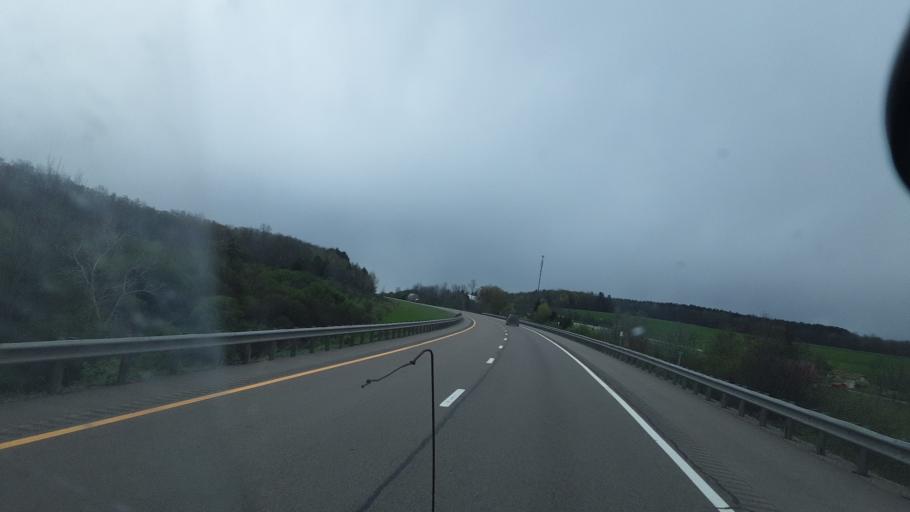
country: US
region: New York
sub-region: Allegany County
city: Alfred
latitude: 42.3166
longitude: -77.8562
